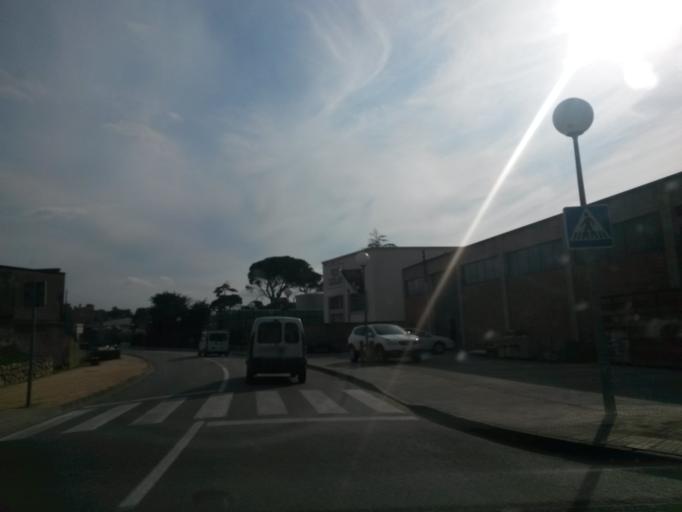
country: ES
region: Catalonia
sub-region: Provincia de Girona
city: Caldes de Malavella
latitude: 41.8389
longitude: 2.8076
